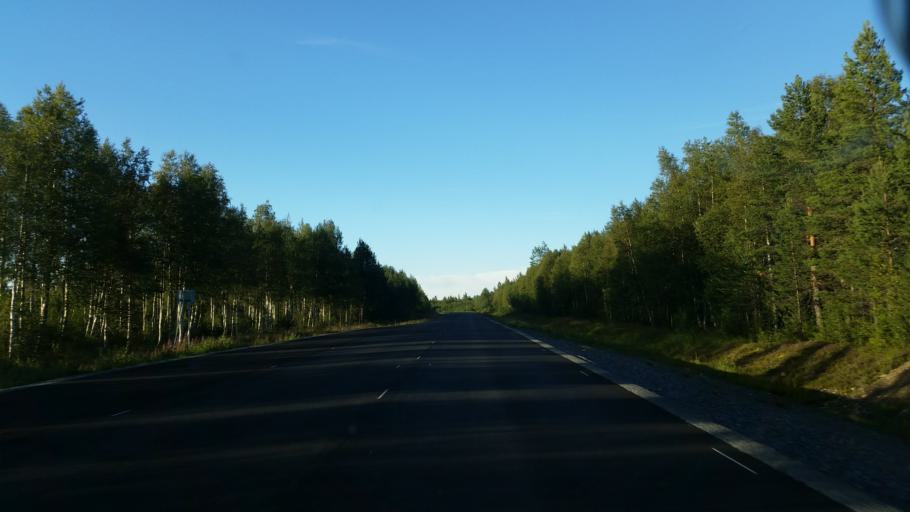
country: SE
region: Vaesterbotten
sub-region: Dorotea Kommun
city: Dorotea
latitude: 64.3319
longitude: 16.6351
